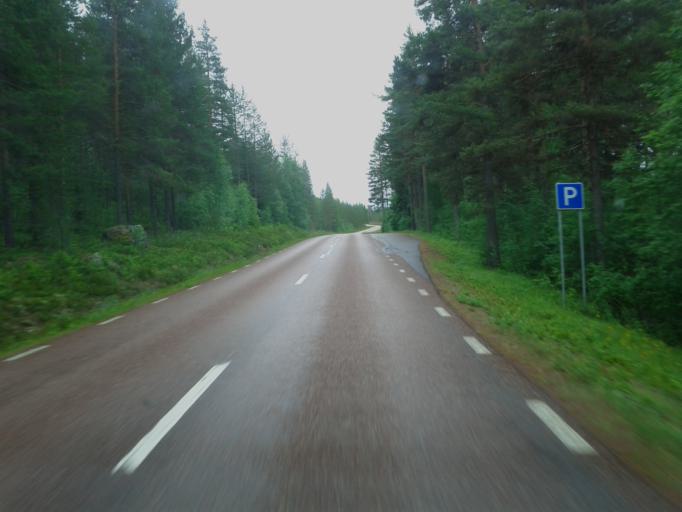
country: NO
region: Hedmark
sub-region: Trysil
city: Innbygda
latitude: 61.7814
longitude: 12.9394
